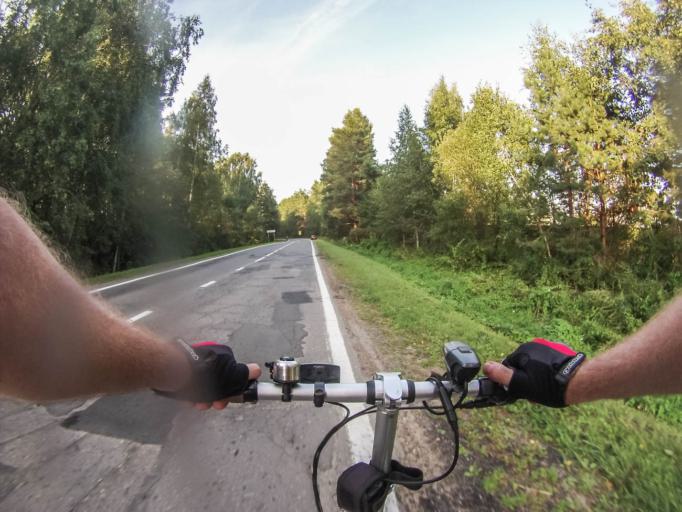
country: RU
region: Jaroslavl
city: Myshkin
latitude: 57.7569
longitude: 38.4426
